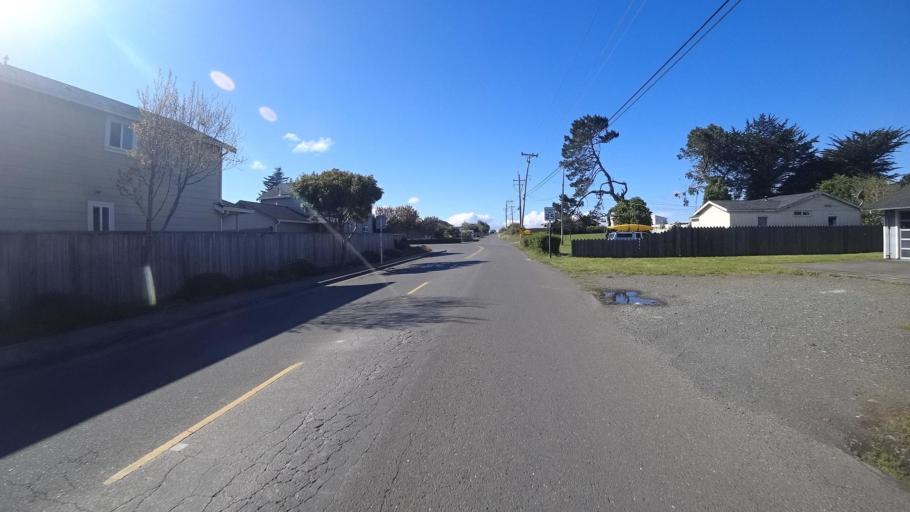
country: US
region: California
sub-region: Humboldt County
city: McKinleyville
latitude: 40.9386
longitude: -124.1107
